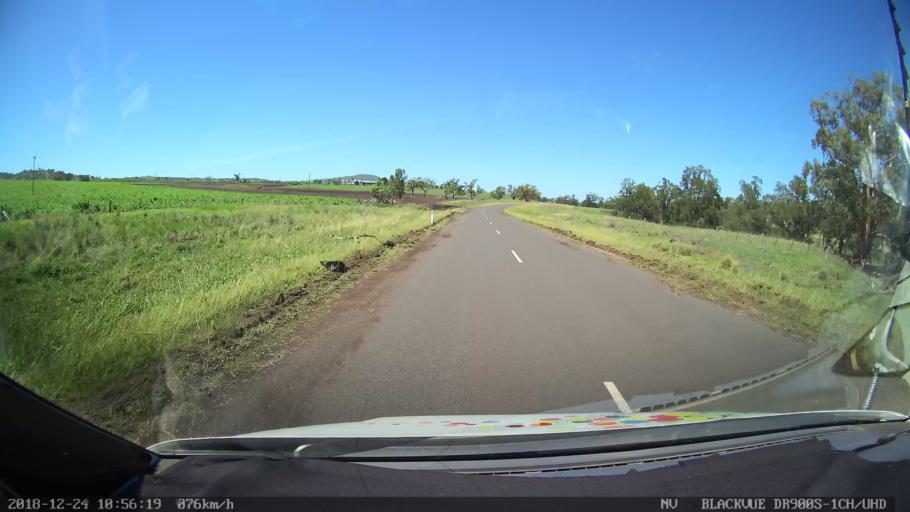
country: AU
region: New South Wales
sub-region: Upper Hunter Shire
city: Merriwa
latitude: -32.0243
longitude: 150.4186
